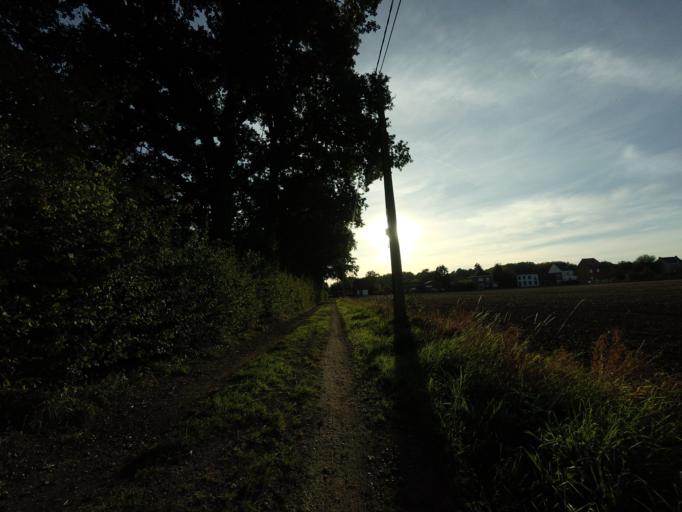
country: BE
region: Flanders
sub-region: Provincie Vlaams-Brabant
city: Kampenhout
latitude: 50.9428
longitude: 4.5903
